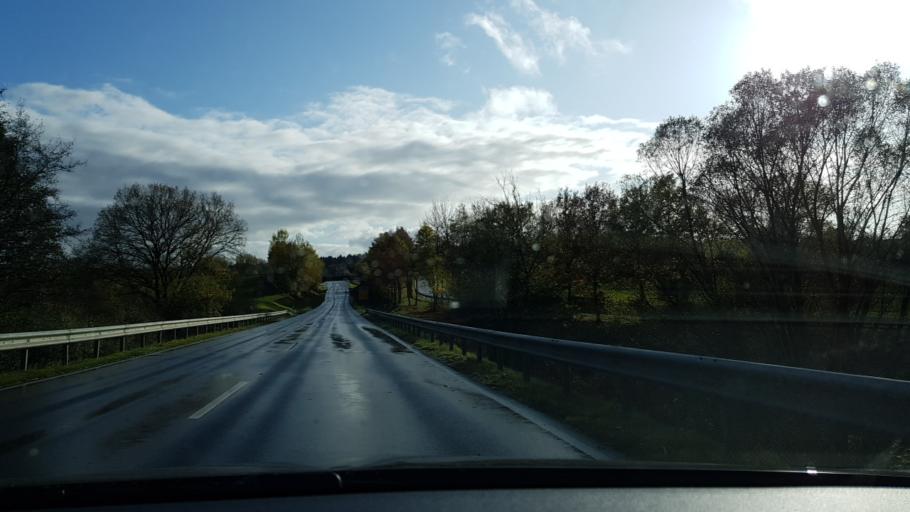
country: DE
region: Rheinland-Pfalz
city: Horschhausen
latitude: 50.2461
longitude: 6.9297
